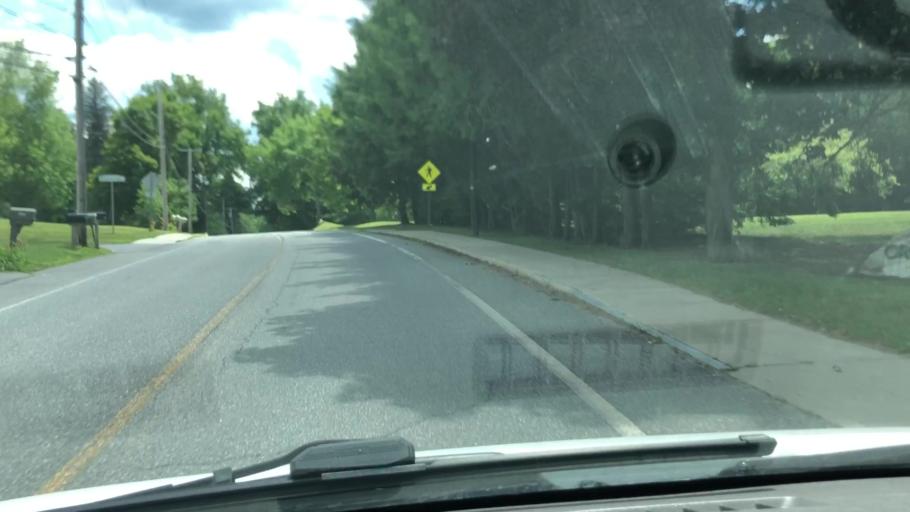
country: US
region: Massachusetts
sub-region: Berkshire County
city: Adams
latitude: 42.6094
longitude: -73.1189
